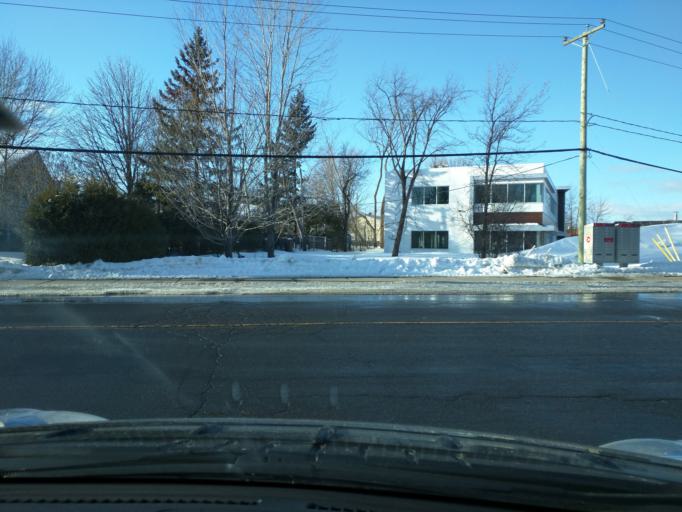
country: CA
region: Quebec
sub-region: Laurentides
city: Rosemere
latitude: 45.5911
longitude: -73.7879
